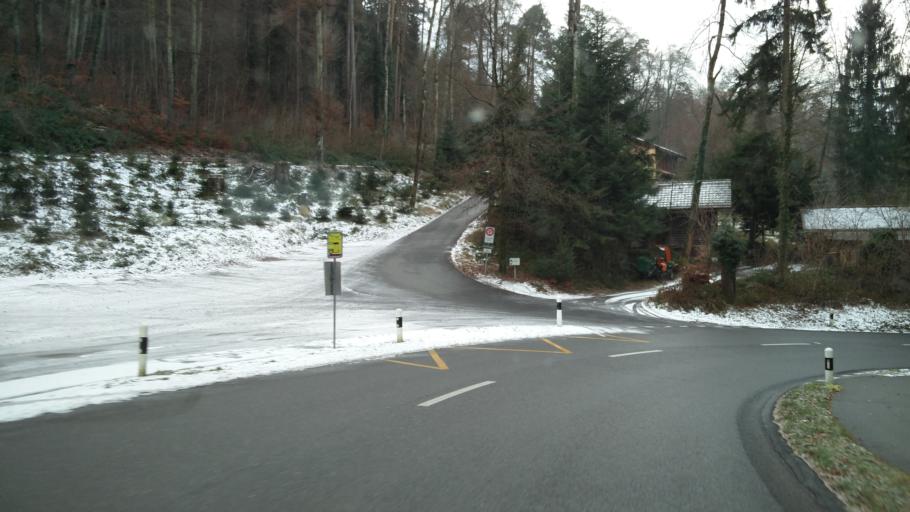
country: LI
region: Planken
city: Planken
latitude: 47.1736
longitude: 9.5342
